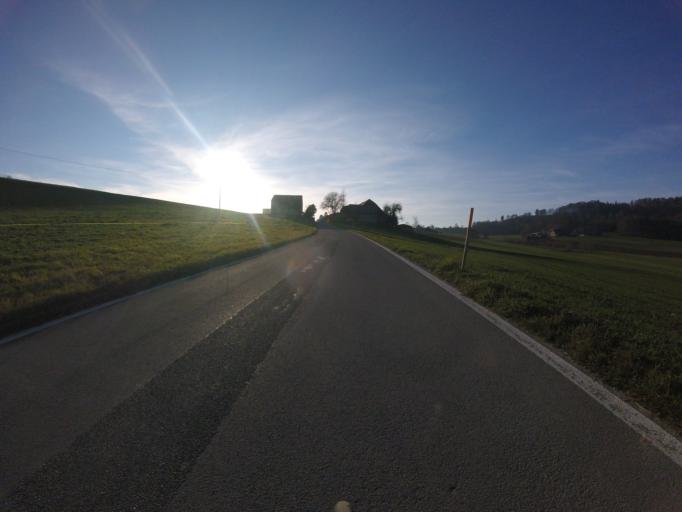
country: CH
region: Bern
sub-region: Bern-Mittelland District
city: Frauenkappelen
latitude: 46.9394
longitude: 7.3020
